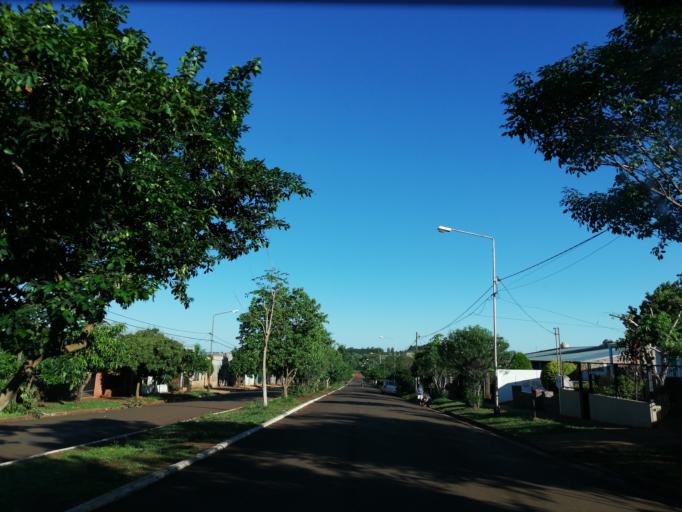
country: AR
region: Misiones
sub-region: Departamento de Capital
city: Posadas
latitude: -27.4353
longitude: -55.9403
